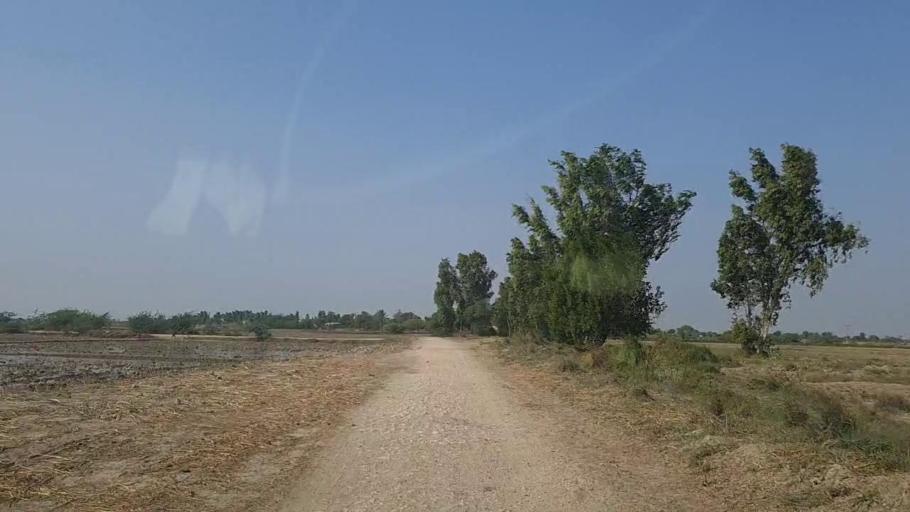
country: PK
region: Sindh
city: Mirpur Sakro
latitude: 24.5667
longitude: 67.8265
